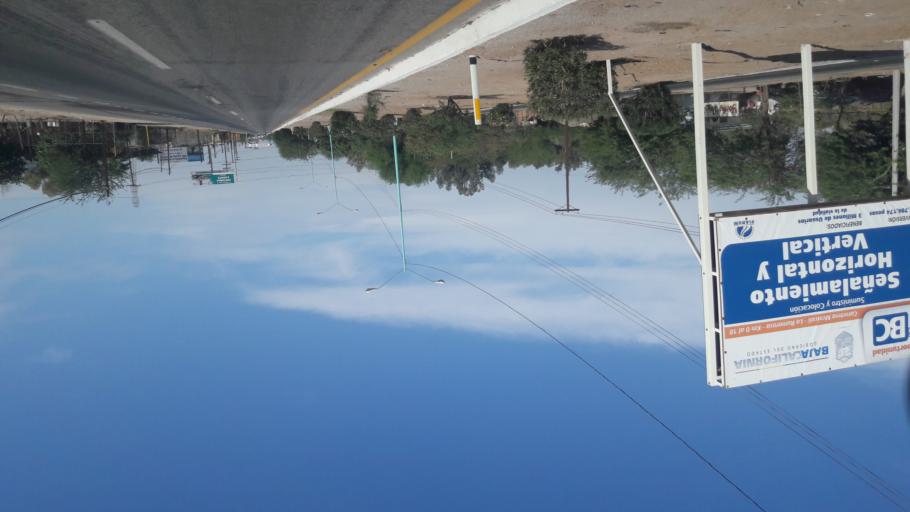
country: MX
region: Baja California
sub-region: Mexicali
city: Vinas del Sol
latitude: 32.6054
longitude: -115.5309
